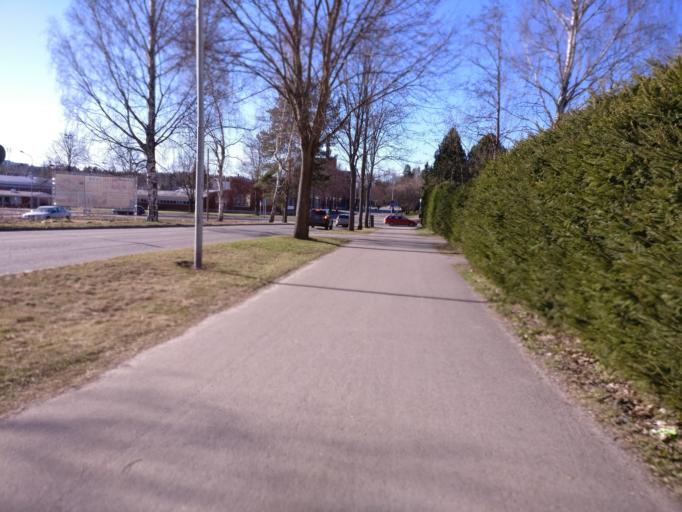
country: FI
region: Uusimaa
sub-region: Helsinki
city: Jaervenpaeae
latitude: 60.4795
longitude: 25.0906
